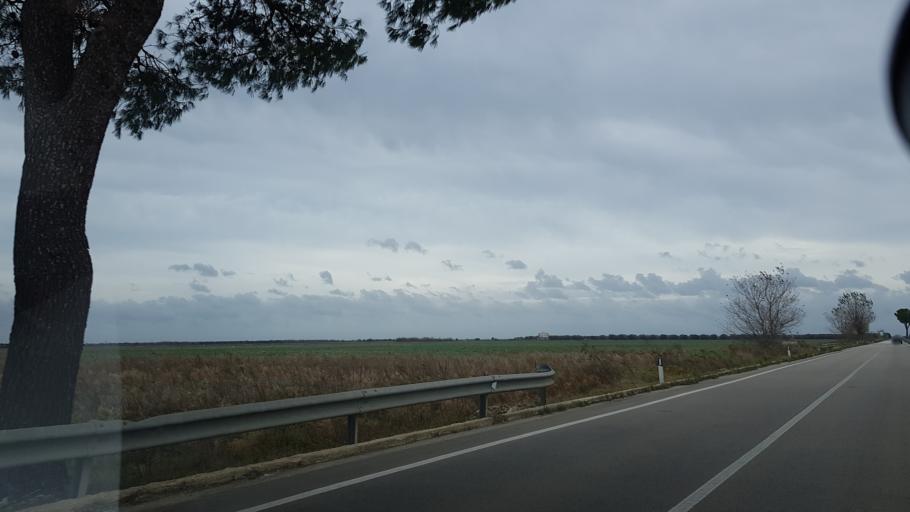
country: IT
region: Apulia
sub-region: Provincia di Brindisi
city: San Pancrazio Salentino
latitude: 40.4113
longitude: 17.8679
